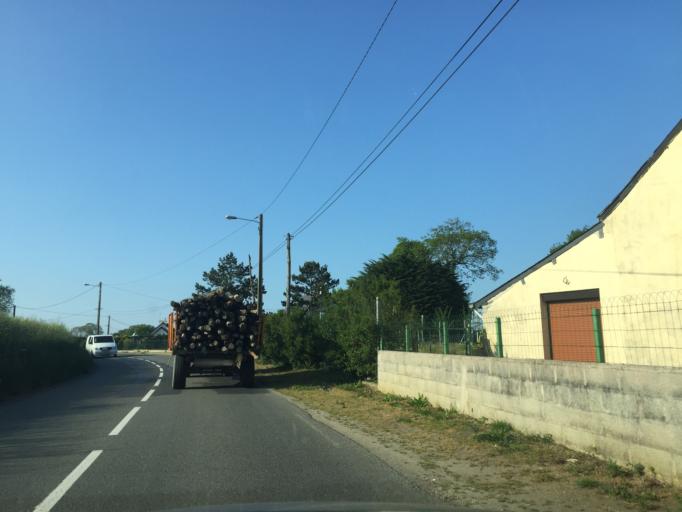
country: FR
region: Brittany
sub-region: Departement des Cotes-d'Armor
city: Saint-Cast-le-Guildo
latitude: 48.6001
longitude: -2.2506
